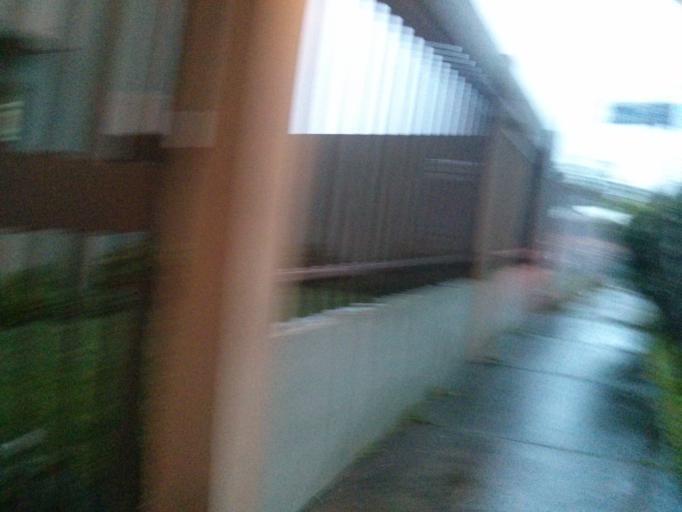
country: CR
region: San Jose
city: San Pedro
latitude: 9.9371
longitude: -84.0554
